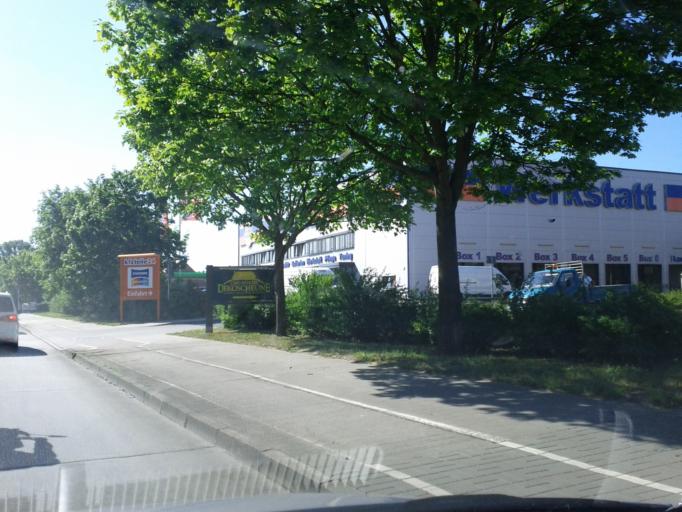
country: DE
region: Berlin
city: Mahlsdorf
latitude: 52.5047
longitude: 13.6185
